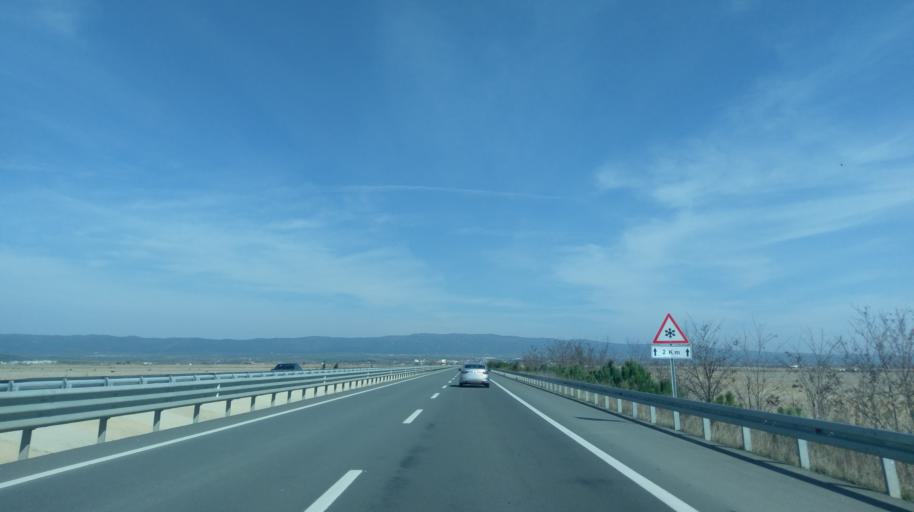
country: TR
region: Canakkale
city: Evrese
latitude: 40.6233
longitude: 26.8680
